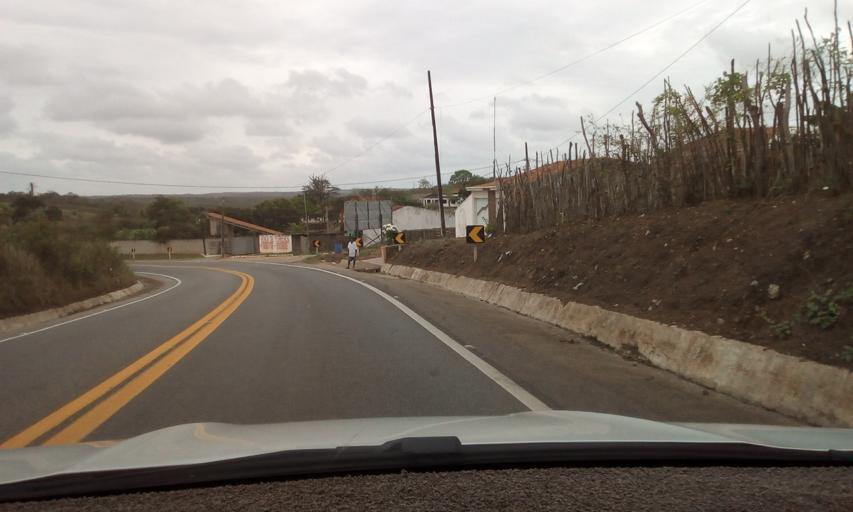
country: BR
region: Paraiba
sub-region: Areia
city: Remigio
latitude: -6.9634
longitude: -35.8001
